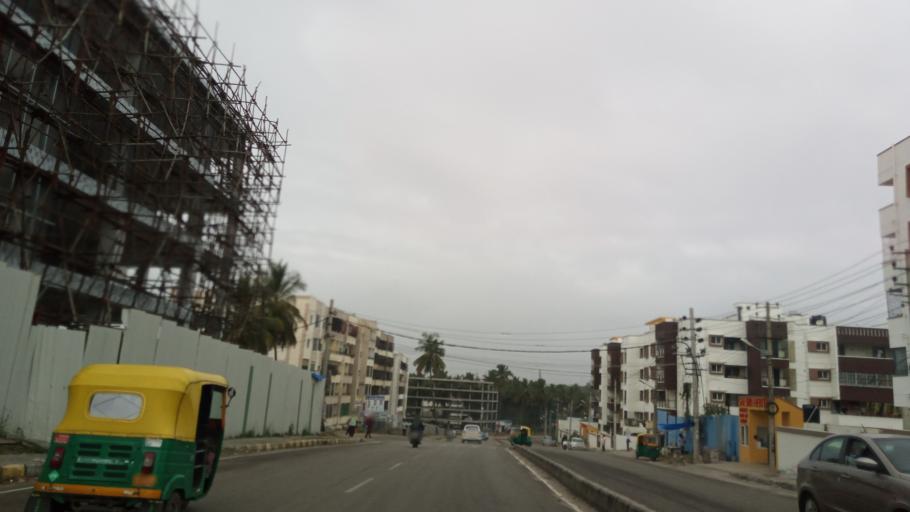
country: IN
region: Karnataka
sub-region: Bangalore Urban
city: Bangalore
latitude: 12.9075
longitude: 77.4895
